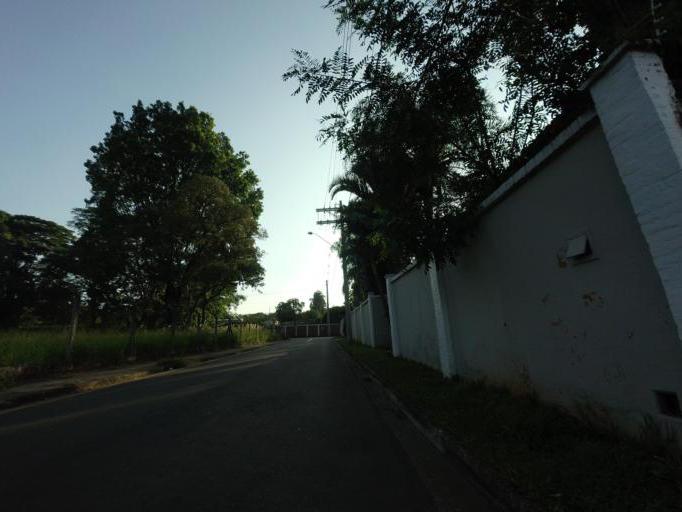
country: BR
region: Sao Paulo
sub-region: Piracicaba
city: Piracicaba
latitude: -22.7439
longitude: -47.6061
